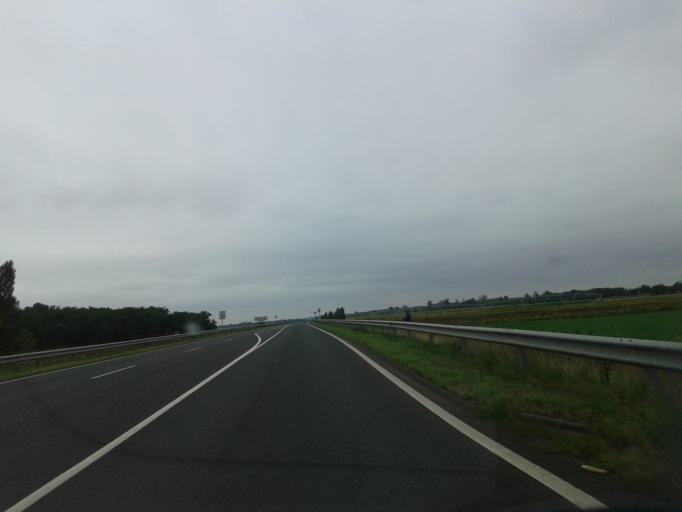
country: HU
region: Bacs-Kiskun
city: Apostag
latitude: 46.8876
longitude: 18.9826
